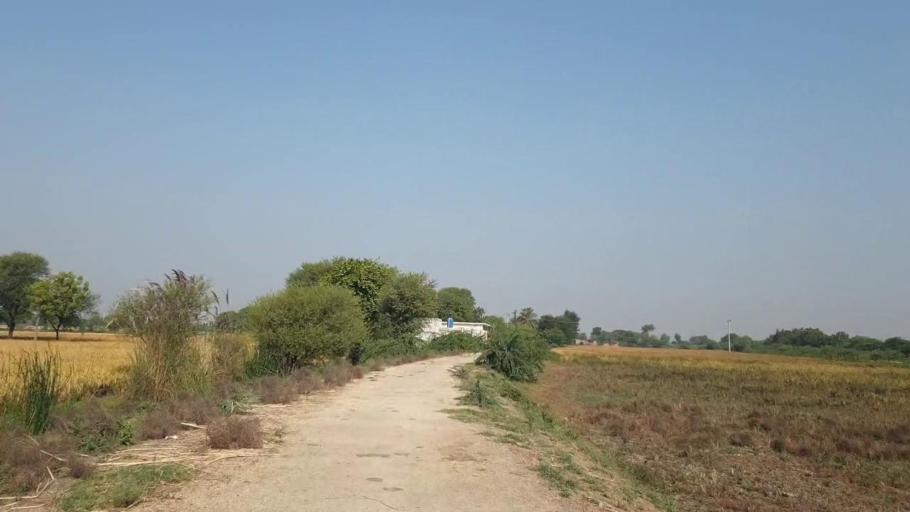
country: PK
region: Sindh
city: Matli
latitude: 25.0000
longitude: 68.6221
